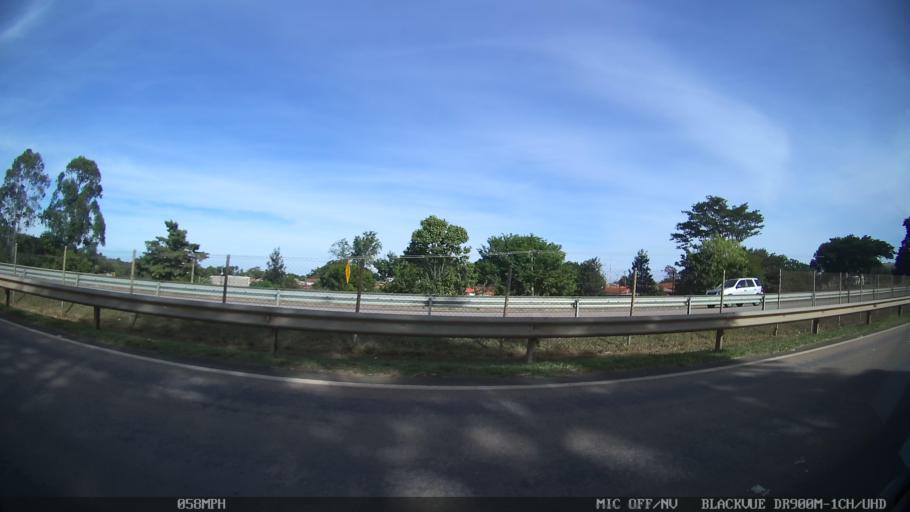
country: BR
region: Sao Paulo
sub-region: Rio Das Pedras
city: Rio das Pedras
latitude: -22.7751
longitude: -47.5915
